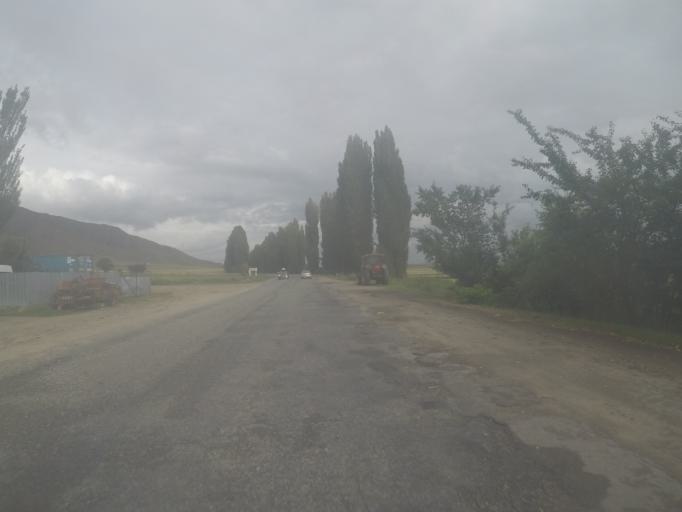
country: KG
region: Ysyk-Koel
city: Tyup
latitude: 42.7420
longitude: 78.0260
